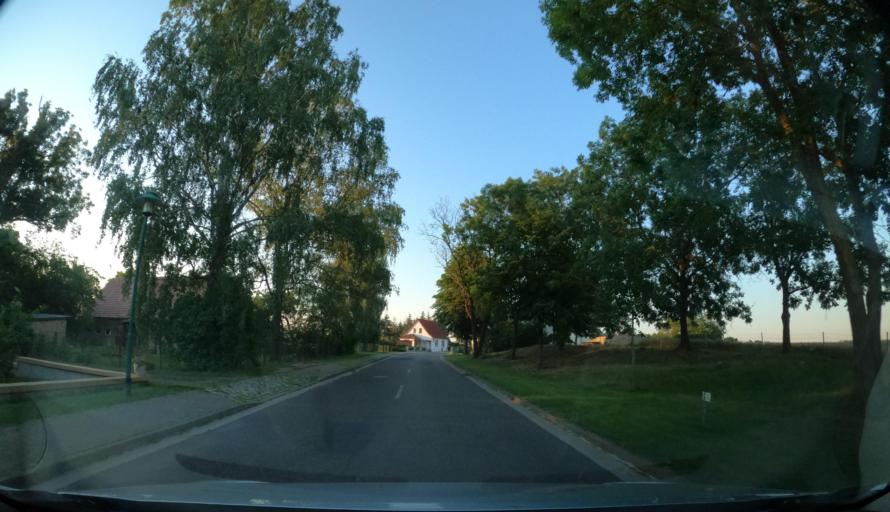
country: DE
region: Brandenburg
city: Tantow
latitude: 53.3048
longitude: 14.3939
